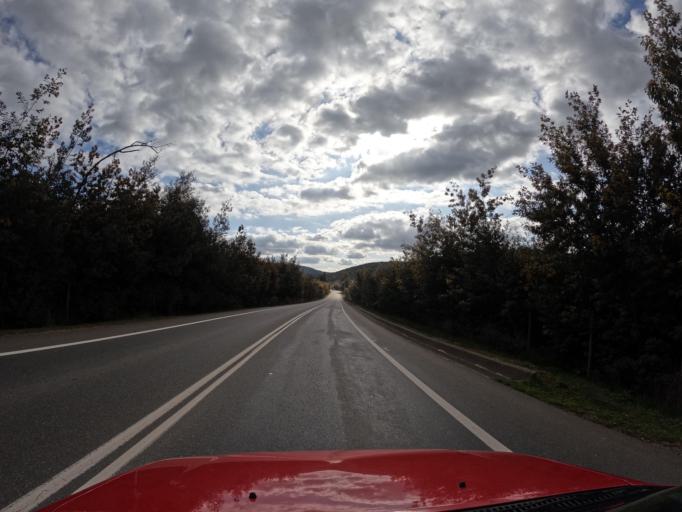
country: CL
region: Maule
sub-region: Provincia de Talca
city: Constitucion
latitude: -35.5564
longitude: -72.1275
